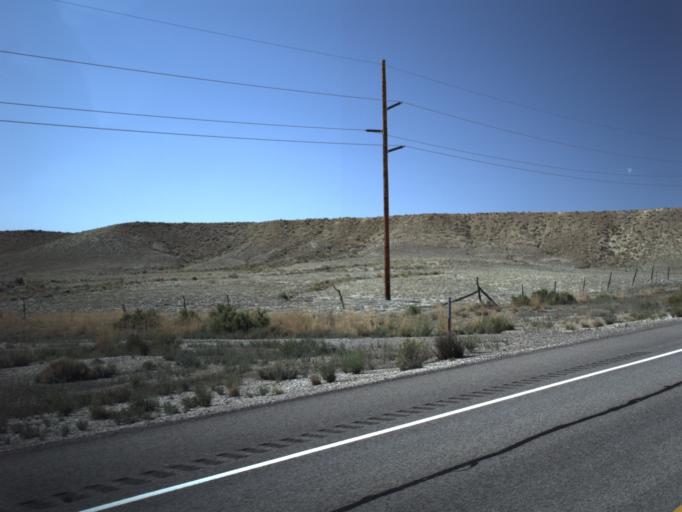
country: US
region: Utah
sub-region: Emery County
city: Ferron
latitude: 38.9358
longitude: -111.2275
